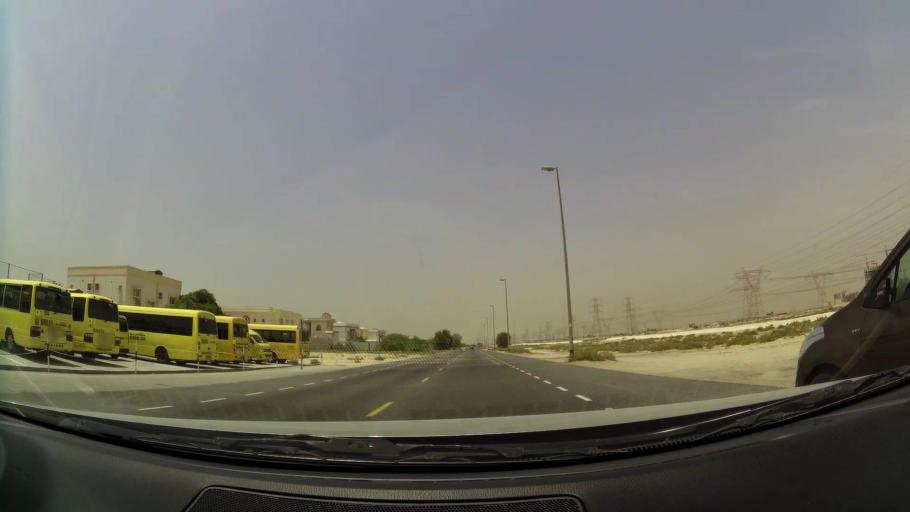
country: AE
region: Ash Shariqah
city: Sharjah
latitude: 25.1938
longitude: 55.3894
